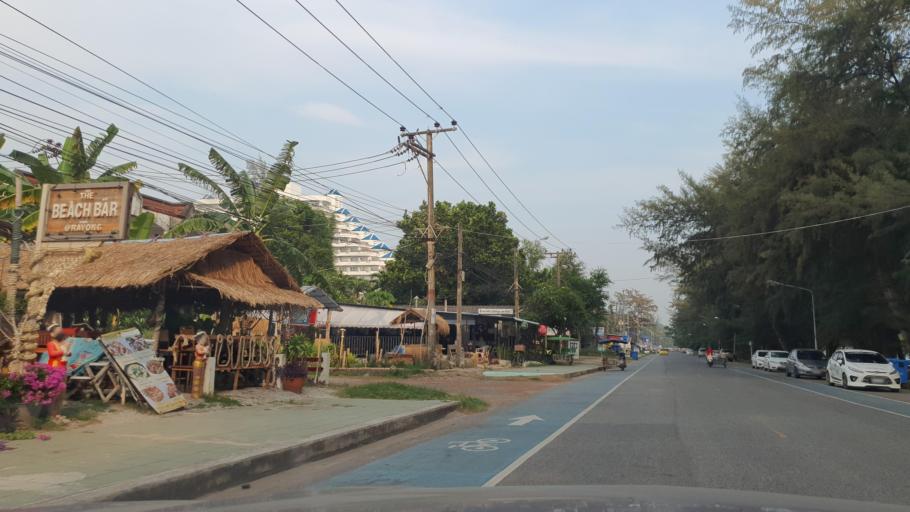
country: TH
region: Rayong
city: Rayong
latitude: 12.6005
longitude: 101.4040
